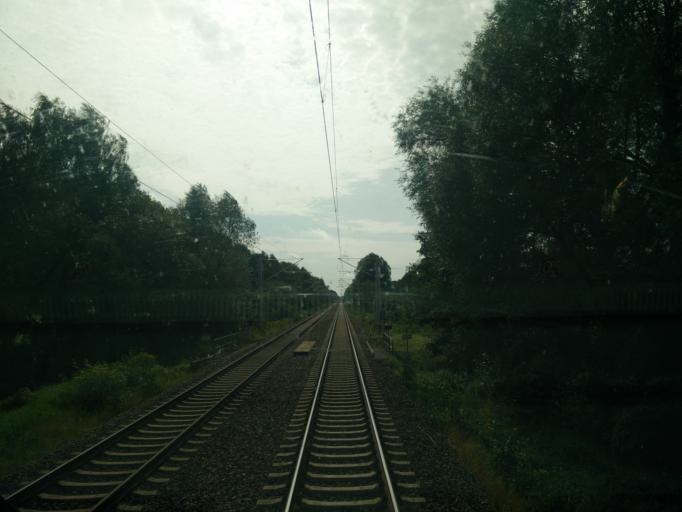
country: DE
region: Brandenburg
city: Luebben
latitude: 51.9045
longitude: 13.9041
